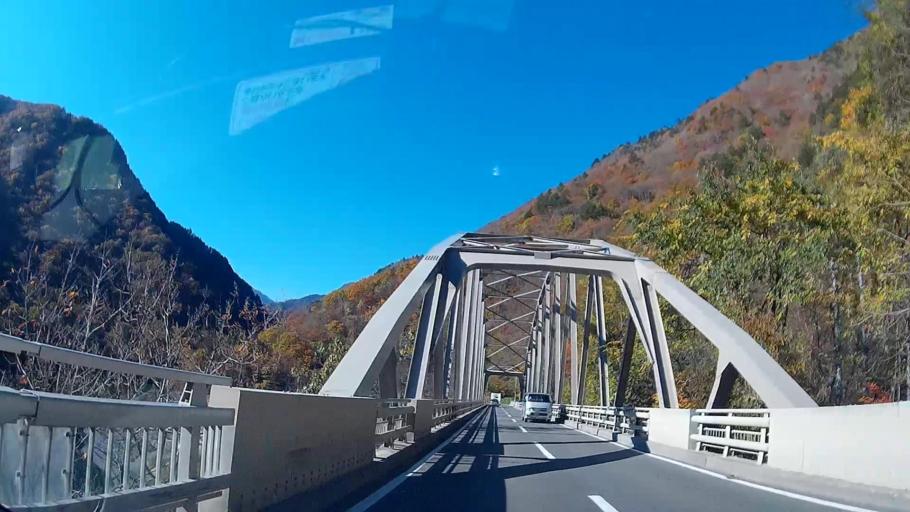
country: JP
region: Nagano
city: Toyoshina
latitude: 36.1584
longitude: 137.6757
